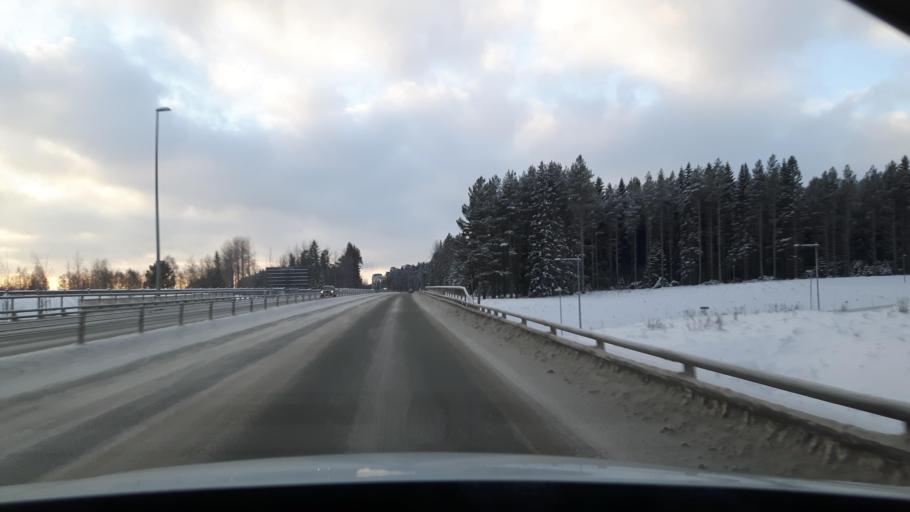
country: SE
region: Vaesterbotten
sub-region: Umea Kommun
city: Ersmark
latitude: 63.8455
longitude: 20.3406
